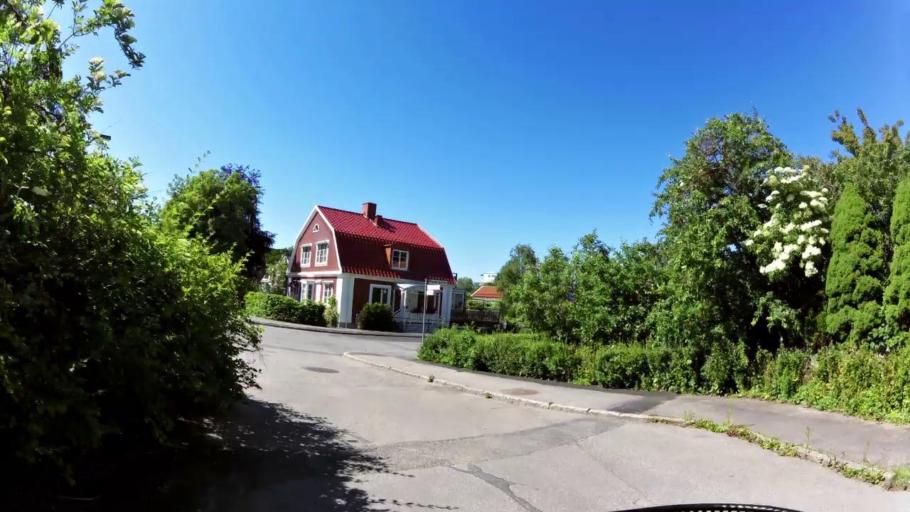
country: SE
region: OEstergoetland
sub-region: Linkopings Kommun
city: Linkoping
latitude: 58.4019
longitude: 15.6281
